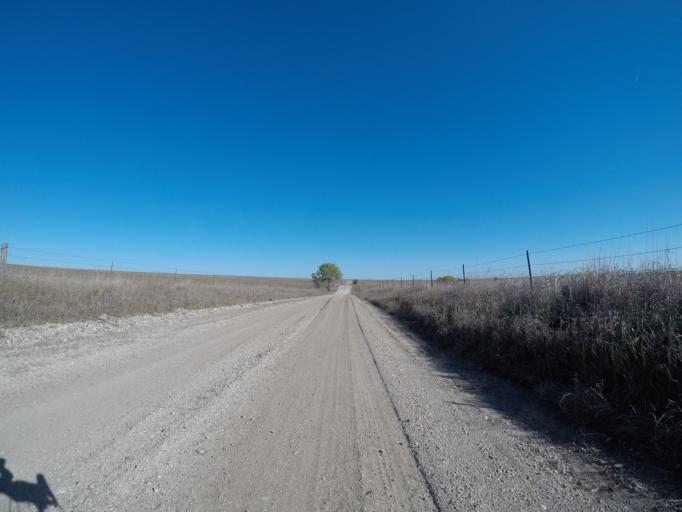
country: US
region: Kansas
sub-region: Wabaunsee County
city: Alma
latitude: 38.8846
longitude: -96.4019
